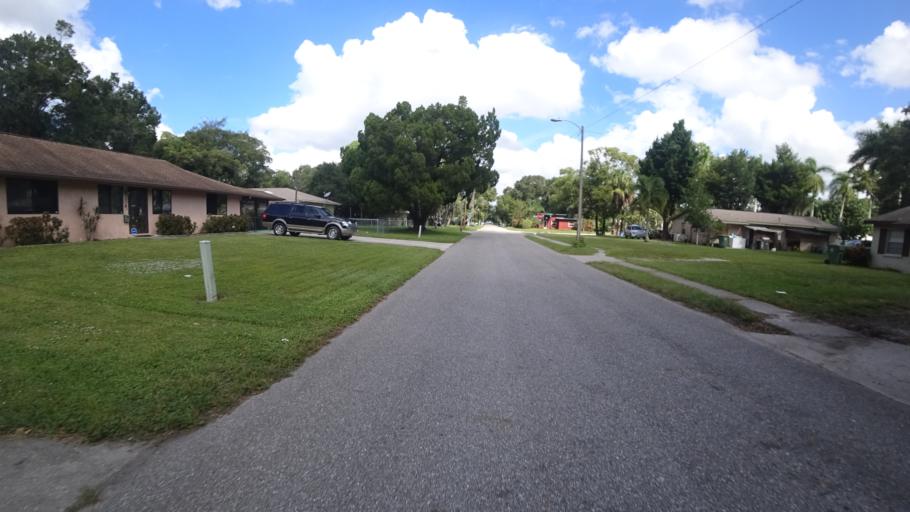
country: US
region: Florida
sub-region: Manatee County
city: Ellenton
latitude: 27.4982
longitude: -82.5344
